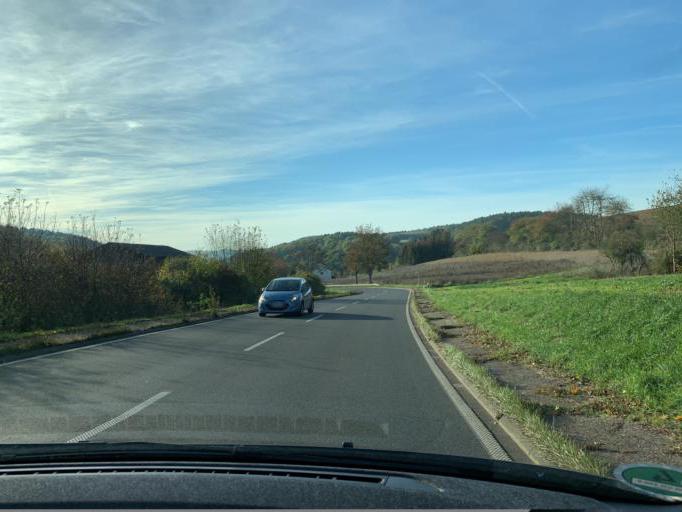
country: DE
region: North Rhine-Westphalia
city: Heimbach
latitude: 50.6385
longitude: 6.5132
